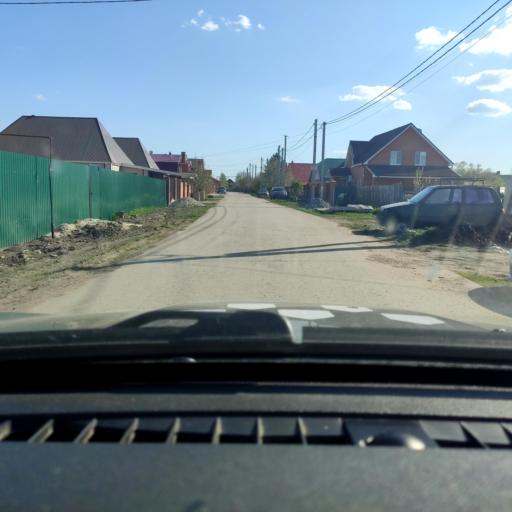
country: RU
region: Samara
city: Tol'yatti
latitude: 53.5639
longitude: 49.3785
